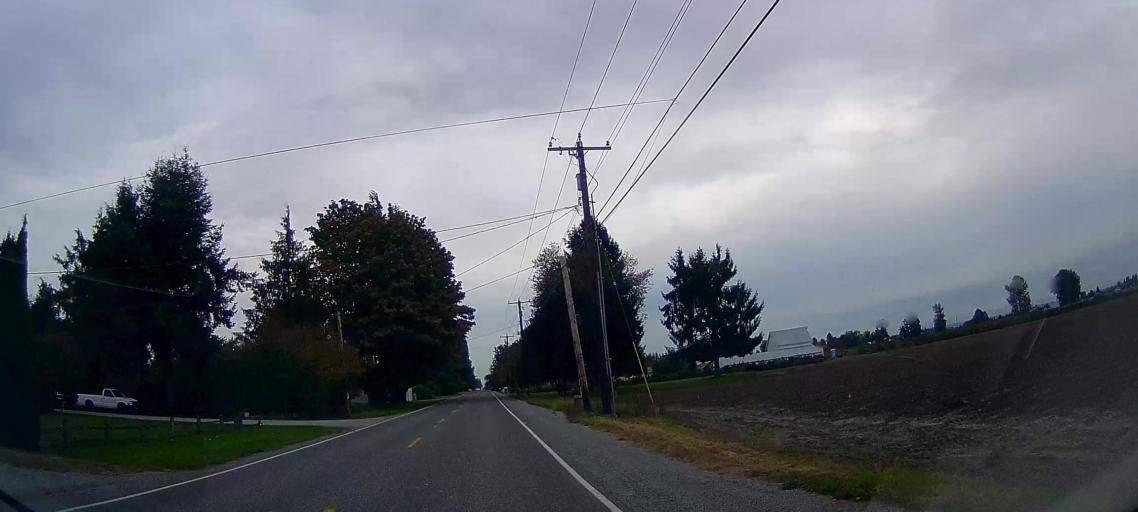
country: US
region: Washington
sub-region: Skagit County
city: Mount Vernon
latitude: 48.4492
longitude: -122.3787
